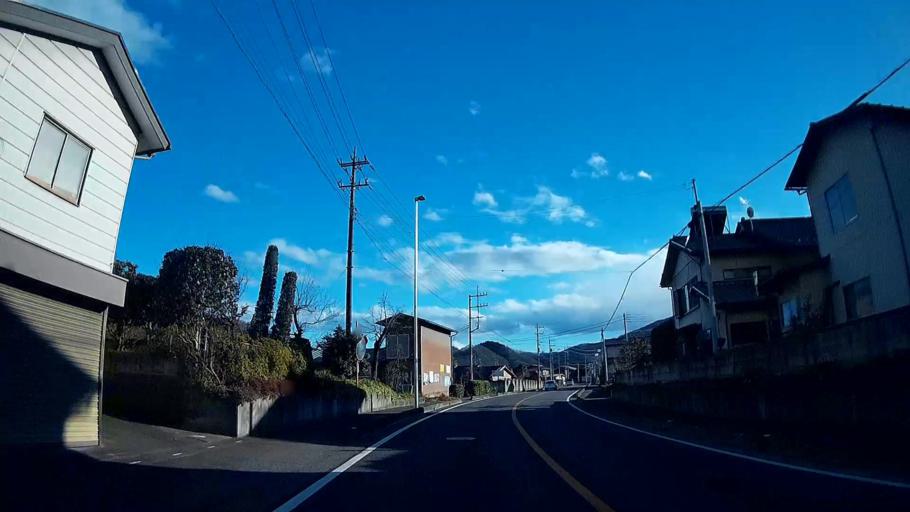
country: JP
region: Saitama
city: Yorii
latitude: 36.0913
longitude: 139.1129
